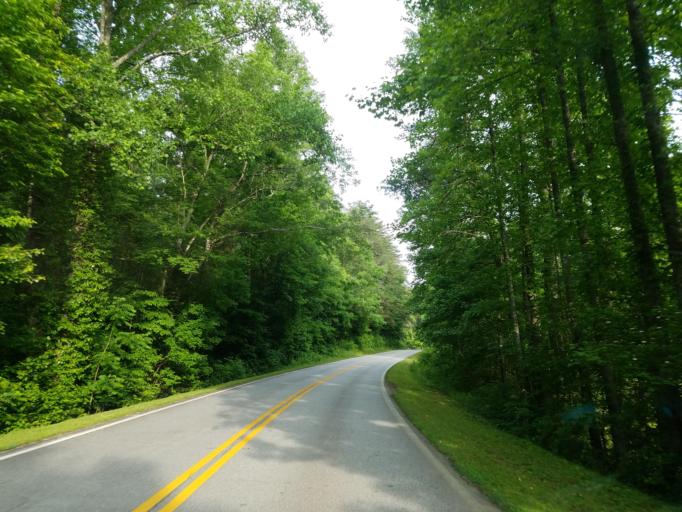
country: US
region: Georgia
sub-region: Lumpkin County
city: Dahlonega
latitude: 34.6108
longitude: -84.0674
